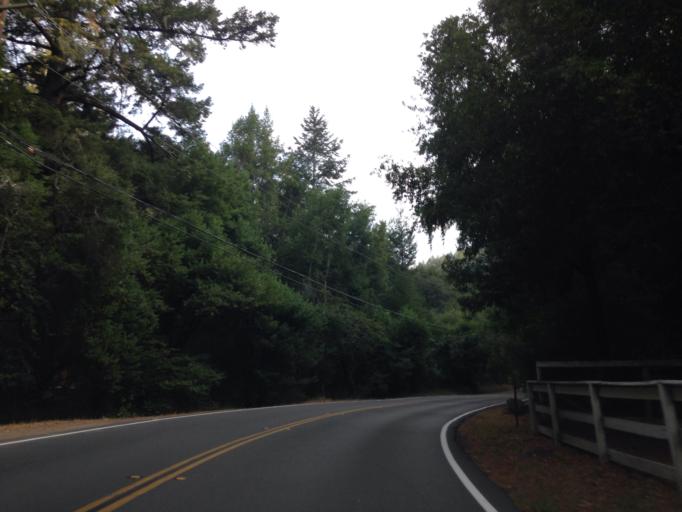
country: US
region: California
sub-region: Marin County
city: Woodacre
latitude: 38.0486
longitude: -122.6434
